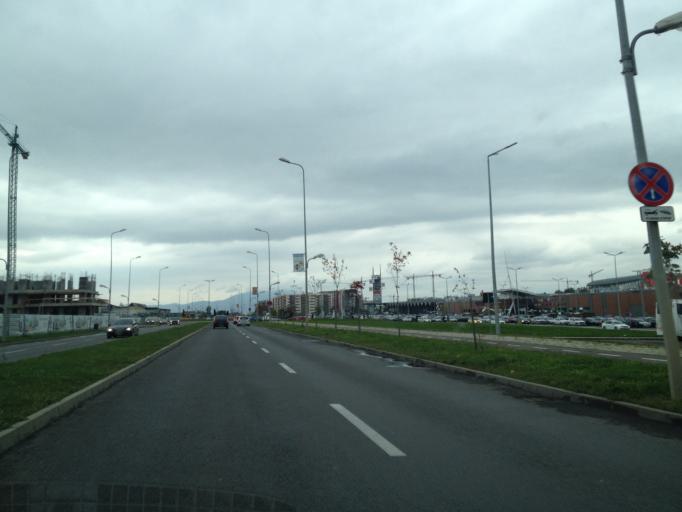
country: RO
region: Brasov
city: Brasov
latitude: 45.6704
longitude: 25.6189
